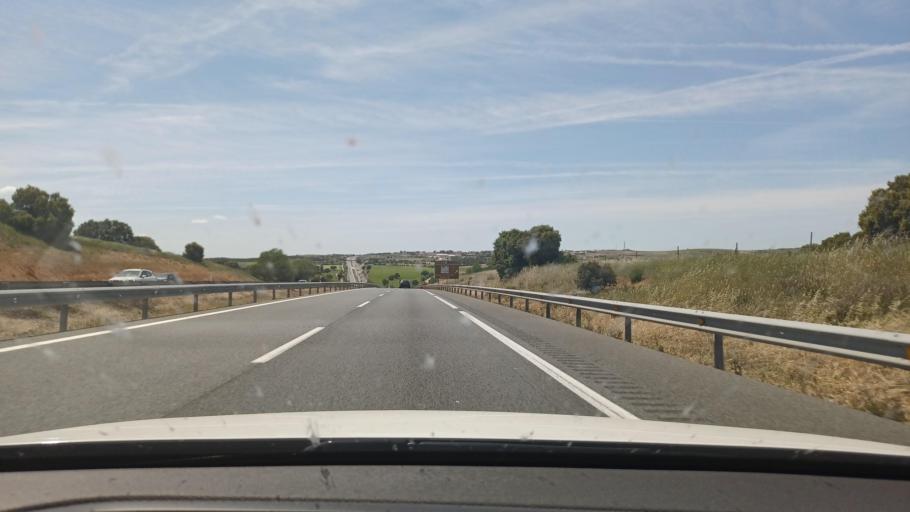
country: ES
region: Castille-La Mancha
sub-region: Provincia de Cuenca
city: Saelices
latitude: 39.9150
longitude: -2.7643
